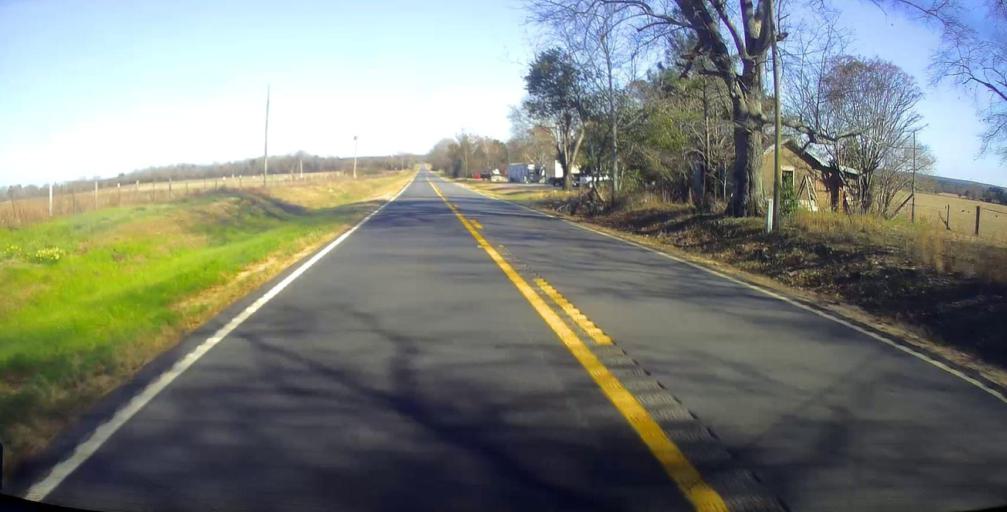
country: US
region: Georgia
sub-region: Taylor County
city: Butler
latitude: 32.6604
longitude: -84.3383
